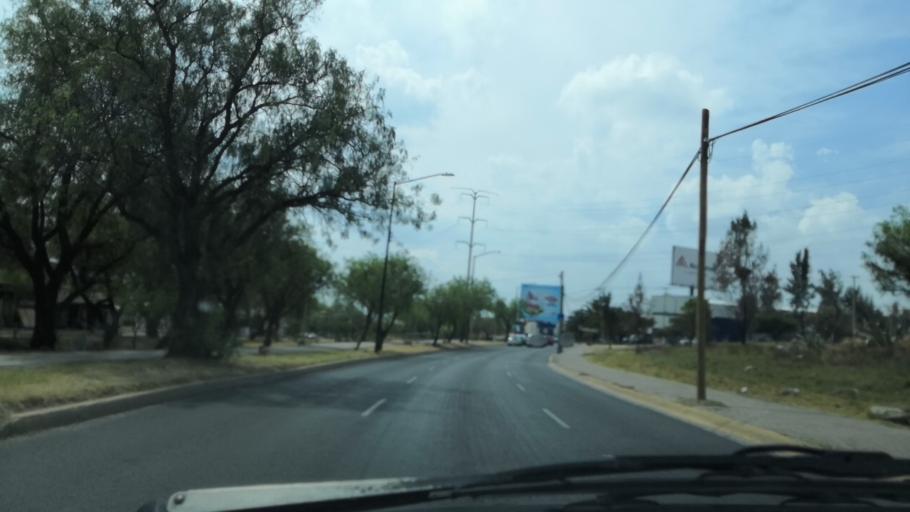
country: MX
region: Guanajuato
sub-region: Leon
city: Ejido la Joya
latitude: 21.1076
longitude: -101.7114
